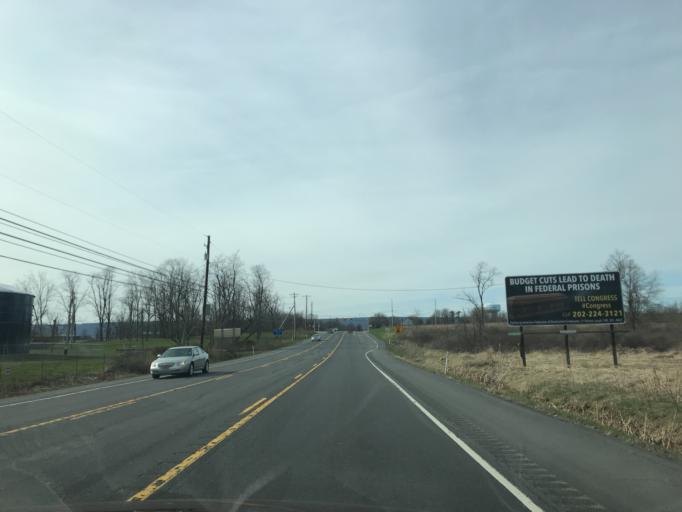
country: US
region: Pennsylvania
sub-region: Northumberland County
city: Dewart
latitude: 41.1261
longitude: -76.9104
